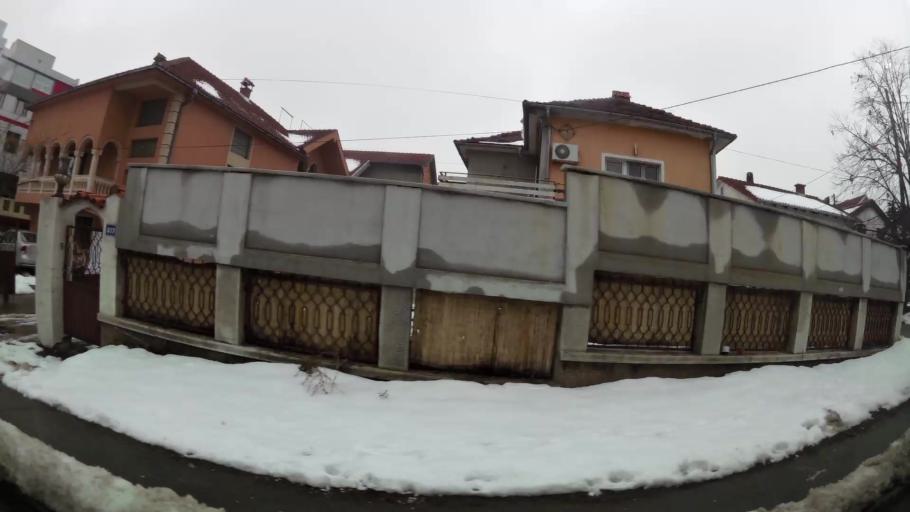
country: RS
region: Central Serbia
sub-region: Belgrade
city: Vozdovac
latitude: 44.7452
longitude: 20.4979
